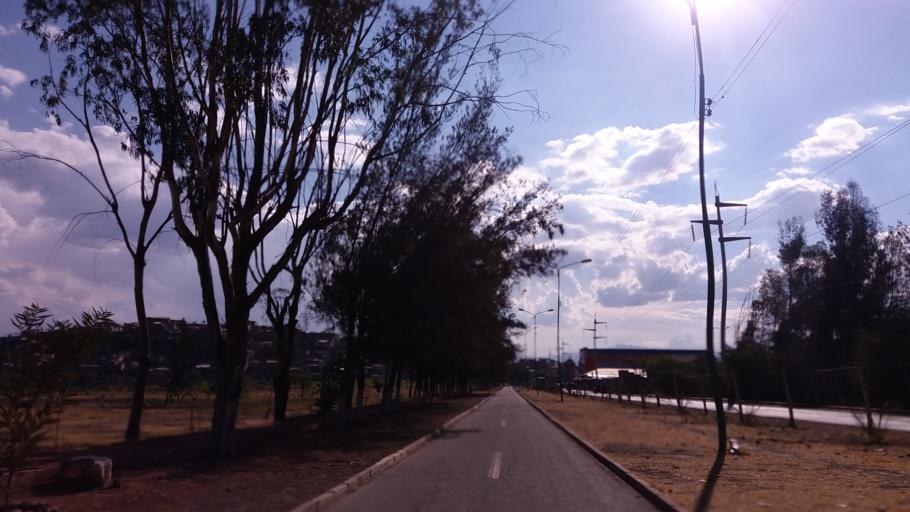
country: BO
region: Cochabamba
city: Cochabamba
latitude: -17.4004
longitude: -66.1405
